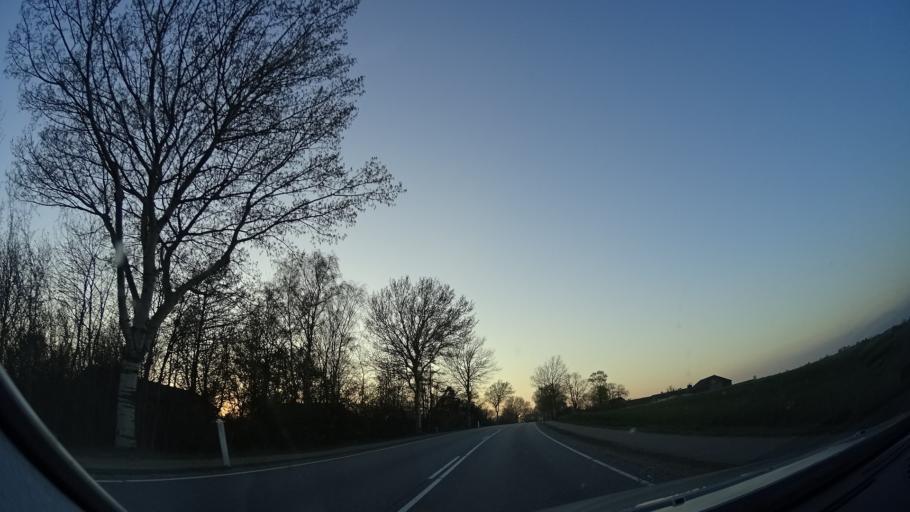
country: DK
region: Zealand
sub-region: Solrod Kommune
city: Havdrup
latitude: 55.5569
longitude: 12.1482
